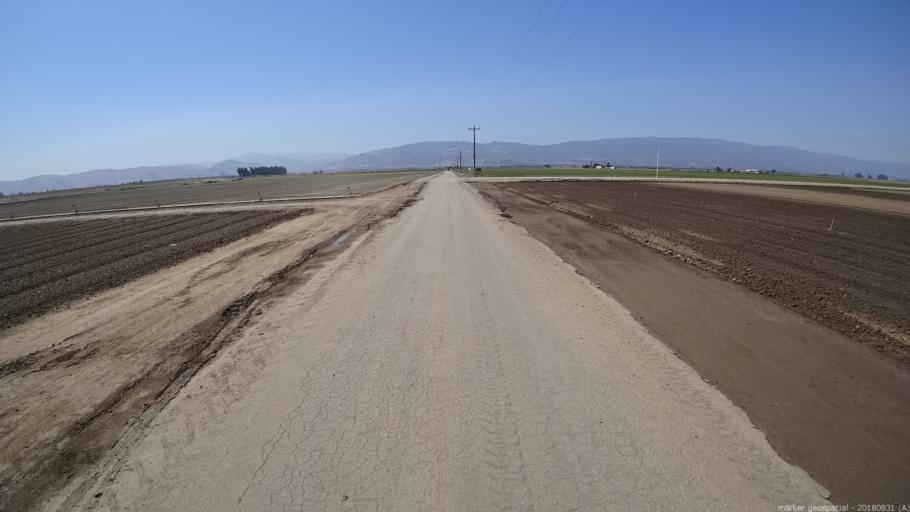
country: US
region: California
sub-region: Monterey County
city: Greenfield
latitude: 36.3561
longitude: -121.2593
